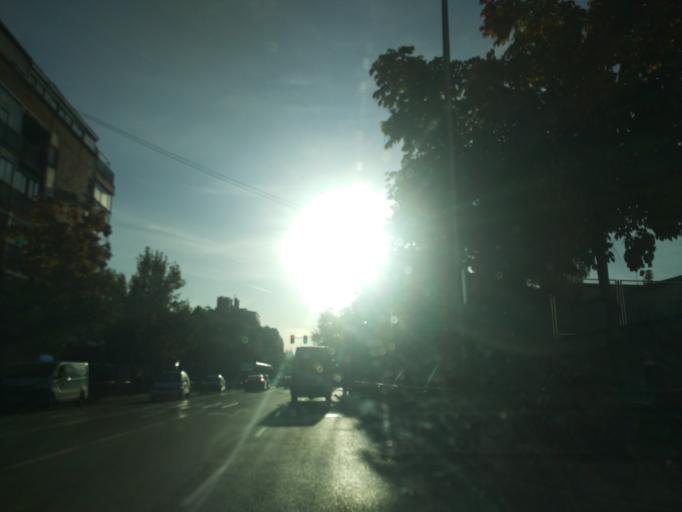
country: ES
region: Madrid
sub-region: Provincia de Madrid
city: Carabanchel
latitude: 40.3891
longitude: -3.7309
